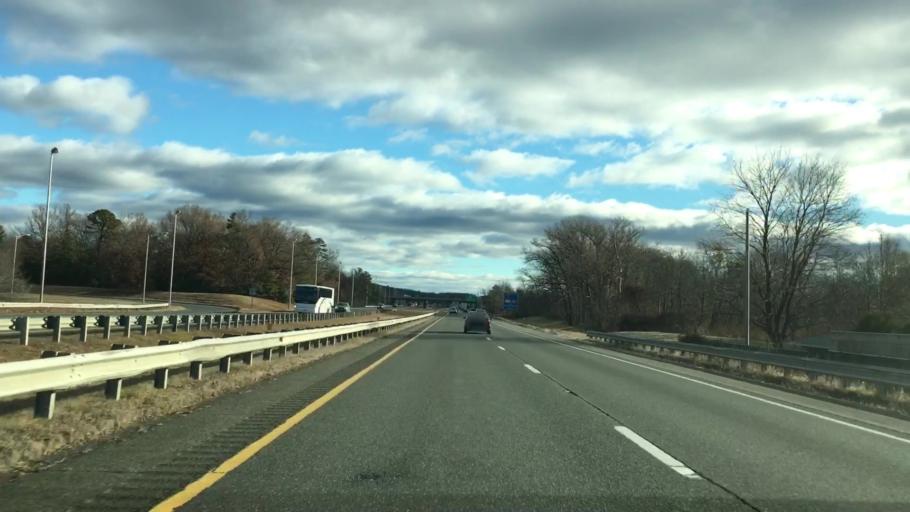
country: US
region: Massachusetts
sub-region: Hampden County
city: Ludlow
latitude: 42.1674
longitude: -72.4788
